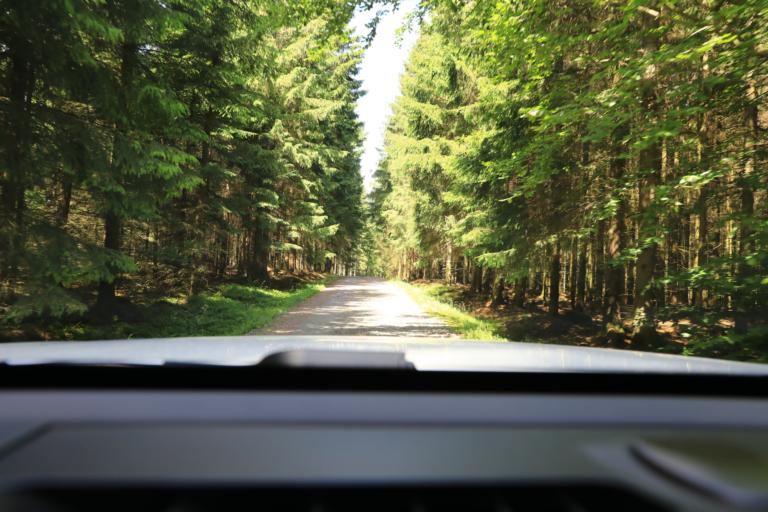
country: SE
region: Halland
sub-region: Varbergs Kommun
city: Tvaaker
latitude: 57.0971
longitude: 12.4833
